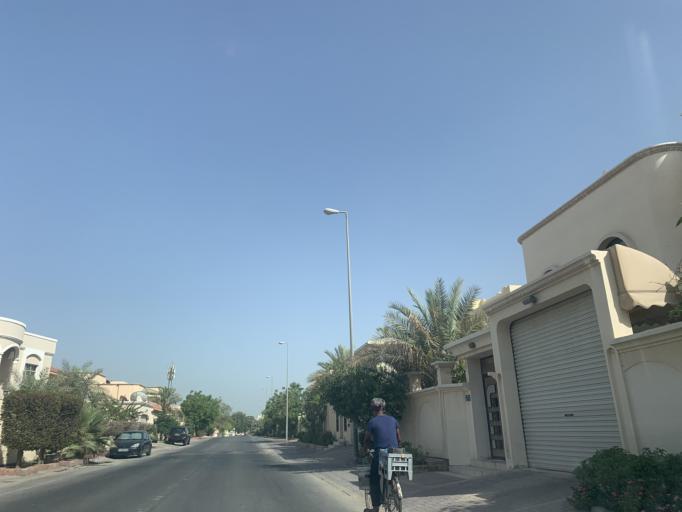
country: BH
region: Northern
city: Madinat `Isa
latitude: 26.1675
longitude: 50.5736
